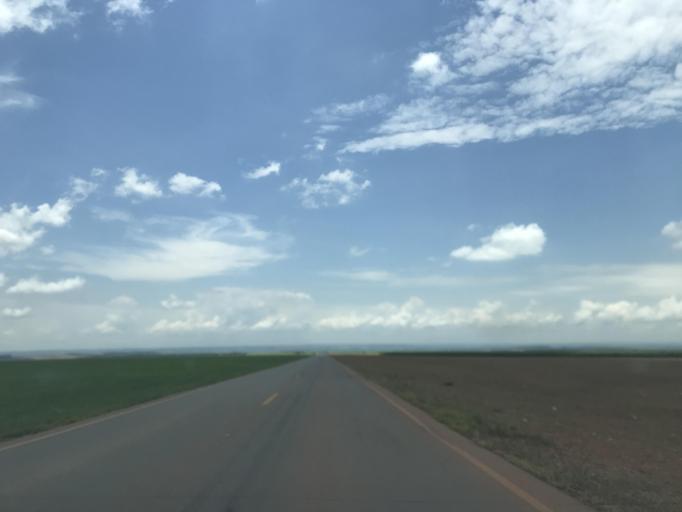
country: BR
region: Goias
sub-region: Vianopolis
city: Vianopolis
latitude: -16.5482
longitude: -48.2675
